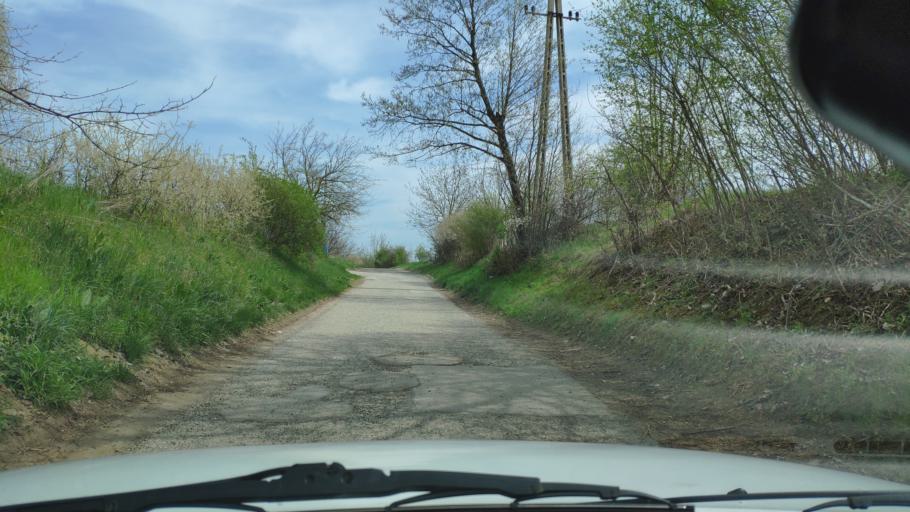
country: HU
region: Zala
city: Nagykanizsa
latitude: 46.4181
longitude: 17.0019
